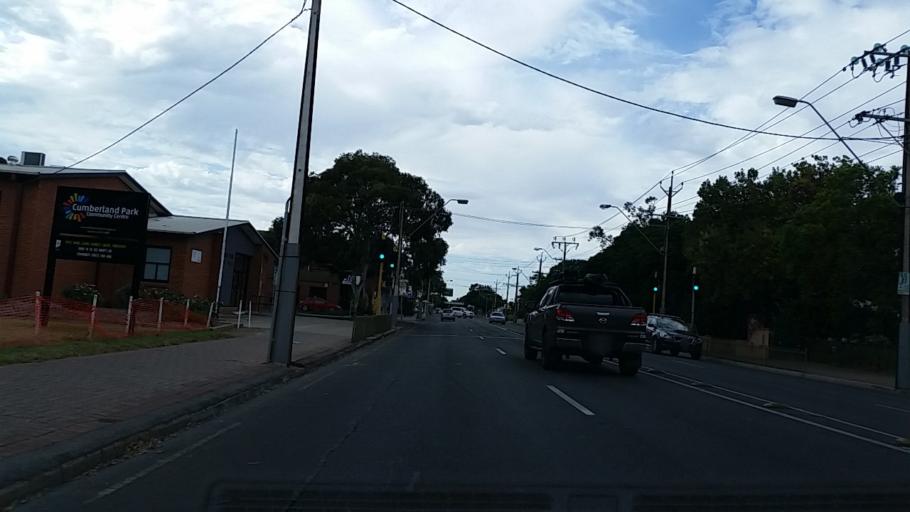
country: AU
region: South Australia
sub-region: Mitcham
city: Clarence Gardens
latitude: -34.9699
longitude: 138.5910
